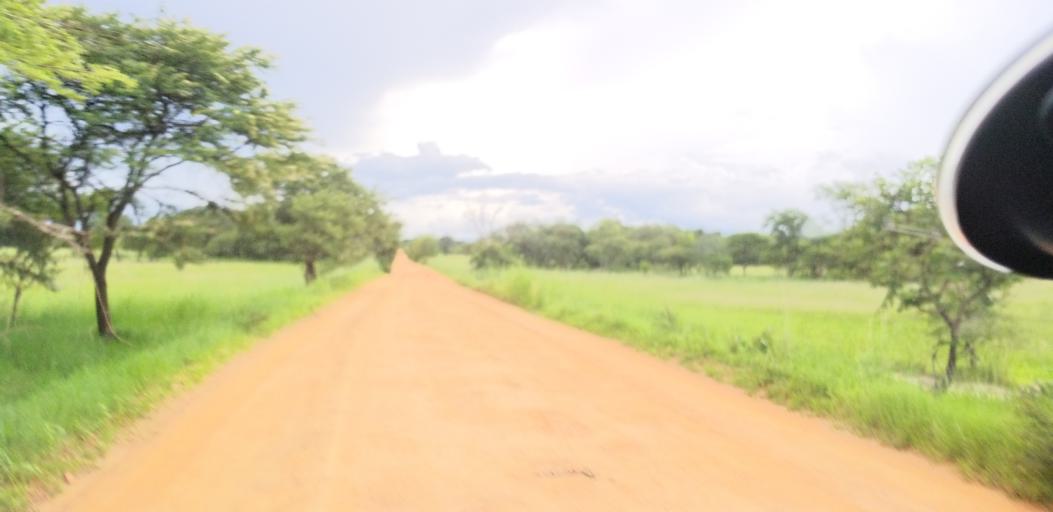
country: ZM
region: Lusaka
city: Chongwe
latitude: -15.1605
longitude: 28.4780
